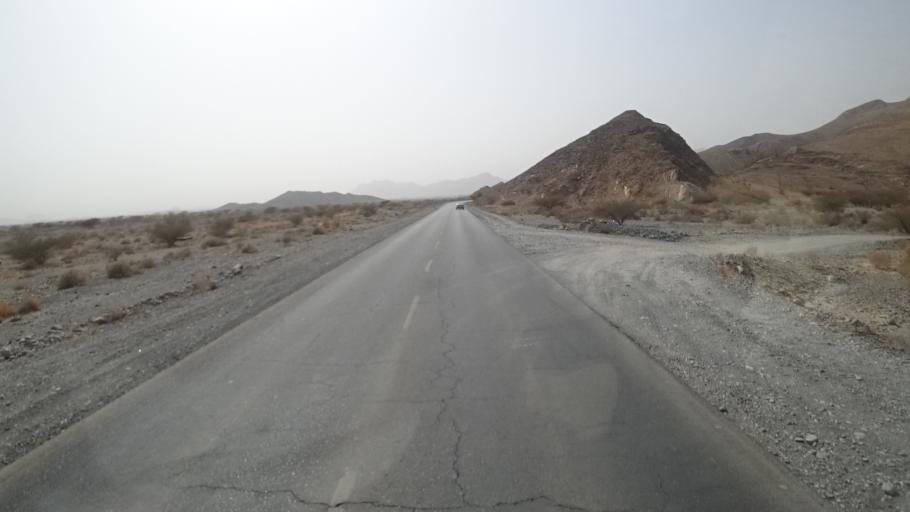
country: OM
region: Muhafazat ad Dakhiliyah
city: Izki
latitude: 22.9248
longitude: 57.6507
